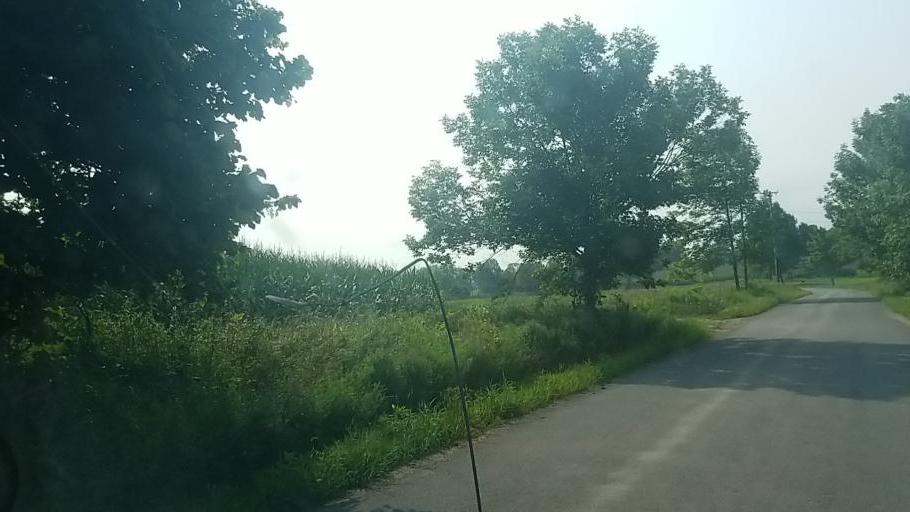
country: US
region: New York
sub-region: Montgomery County
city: Fonda
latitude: 42.9783
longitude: -74.4458
